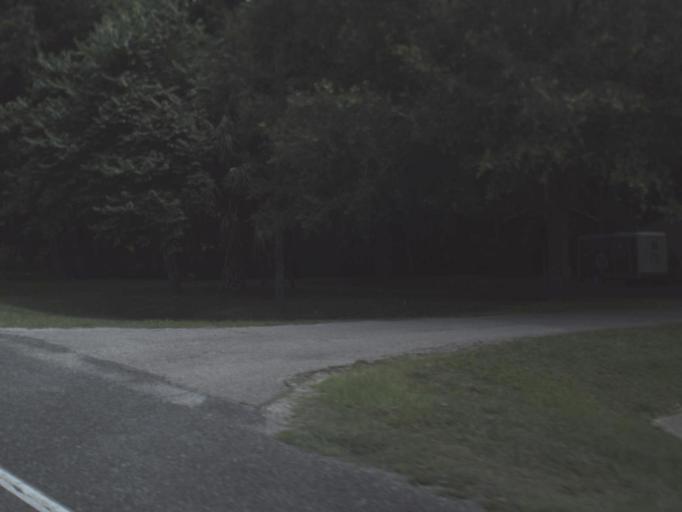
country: US
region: Florida
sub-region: Alachua County
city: Gainesville
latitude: 29.6020
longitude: -82.3409
